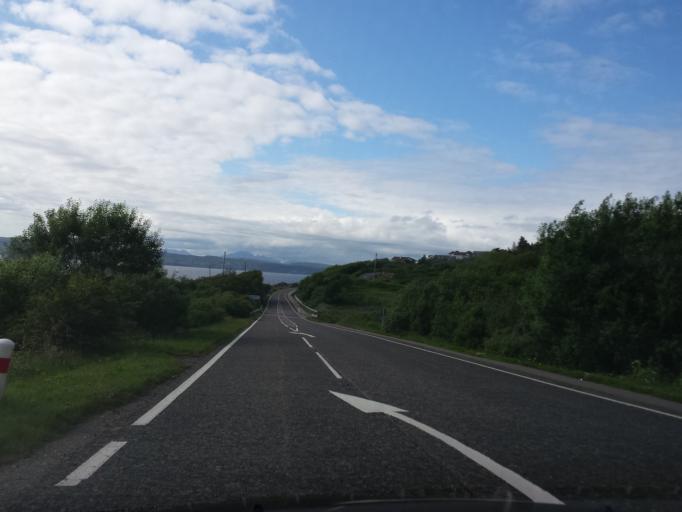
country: GB
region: Scotland
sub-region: Argyll and Bute
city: Isle Of Mull
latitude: 56.9915
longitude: -5.8278
